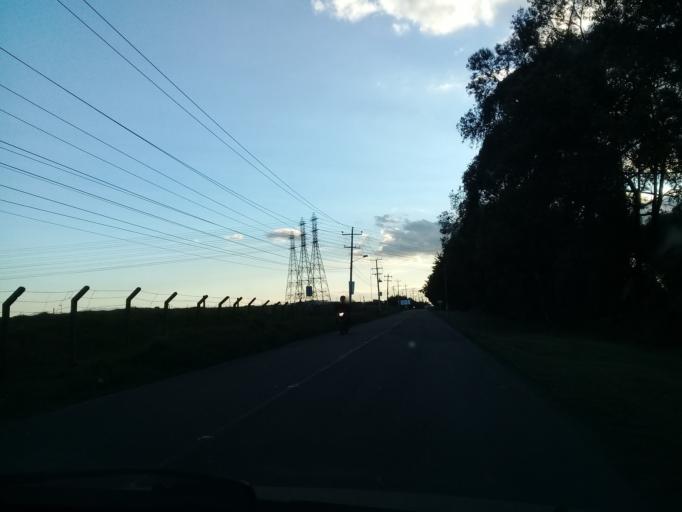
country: CO
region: Cundinamarca
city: Cota
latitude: 4.7819
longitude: -74.1578
